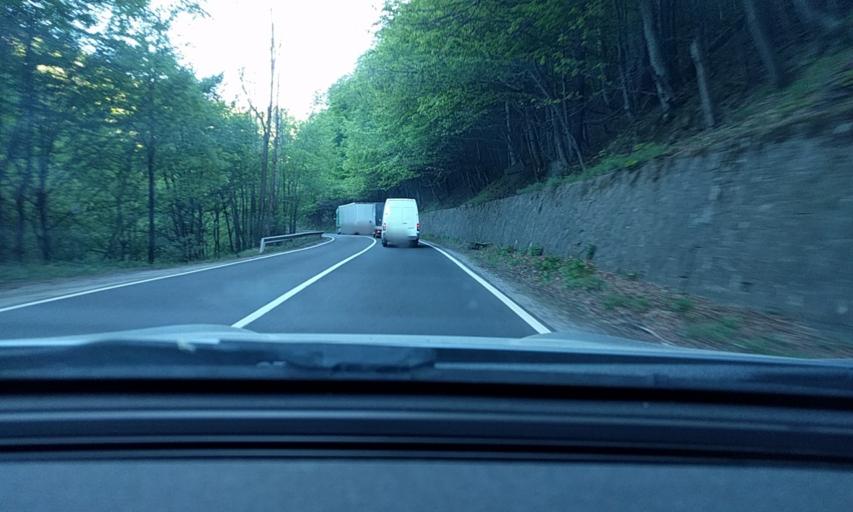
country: RO
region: Covasna
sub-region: Comuna Bretcu
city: Bretcu
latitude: 46.0916
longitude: 26.4048
